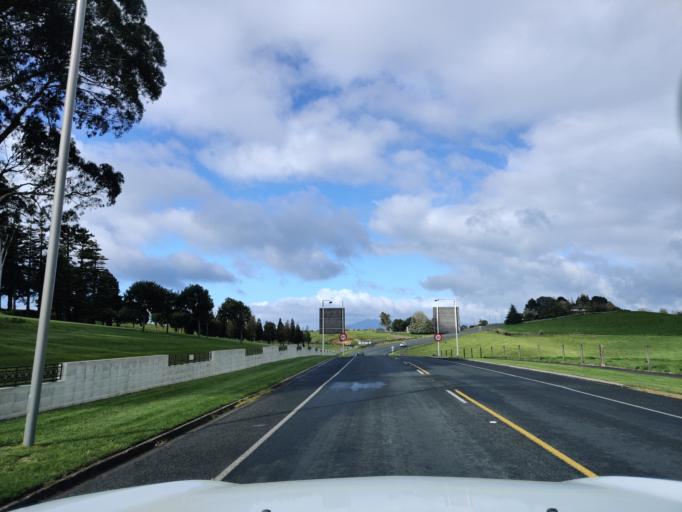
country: NZ
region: Waikato
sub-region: Hamilton City
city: Hamilton
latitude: -37.8263
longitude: 175.2234
